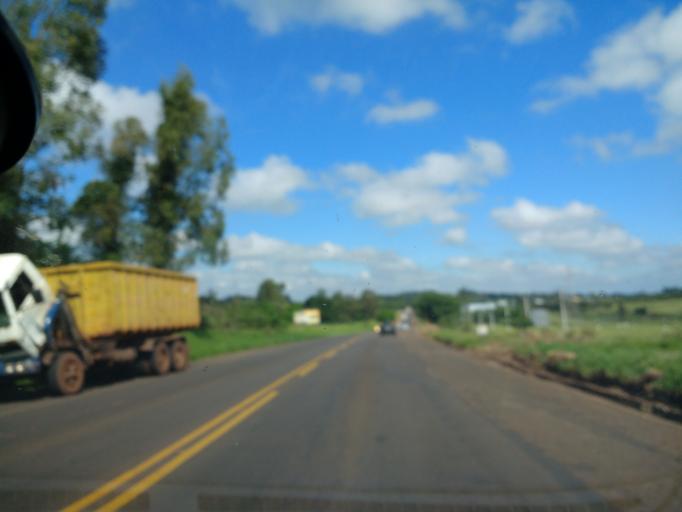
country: BR
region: Parana
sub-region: Cianorte
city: Cianorte
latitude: -23.7216
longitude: -52.6657
